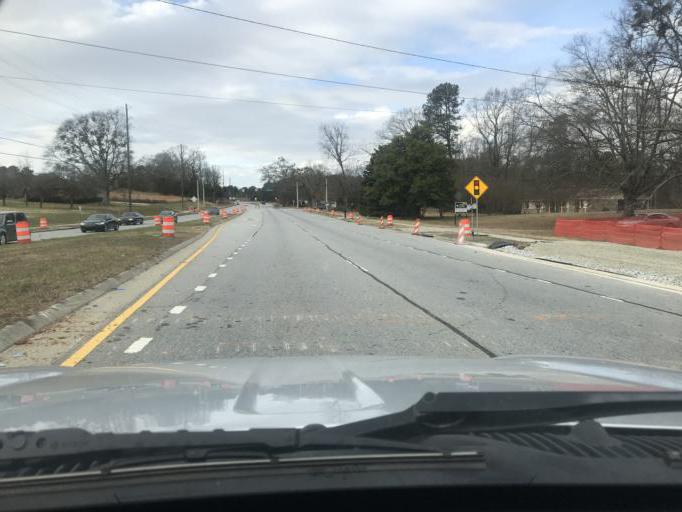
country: US
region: Georgia
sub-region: Gwinnett County
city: Buford
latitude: 34.0643
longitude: -83.9481
